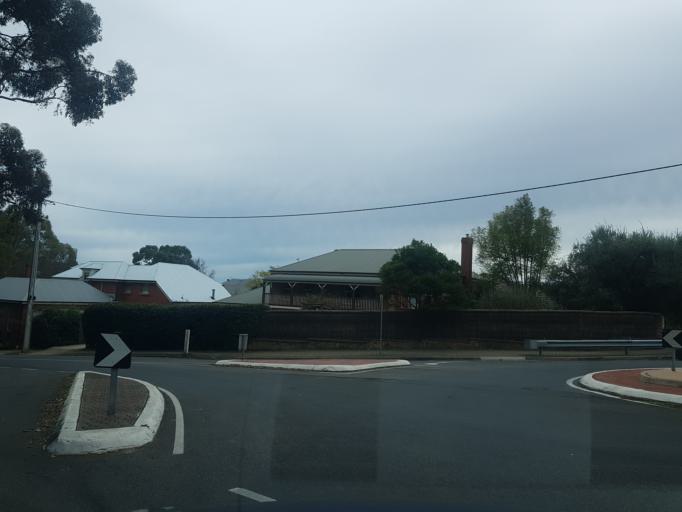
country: AU
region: South Australia
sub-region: Burnside
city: Mount Osmond
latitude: -34.9572
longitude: 138.6527
